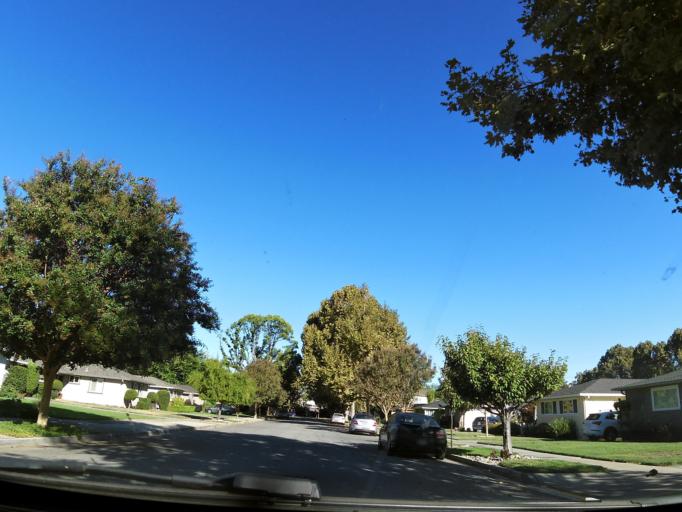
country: US
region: California
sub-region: Santa Clara County
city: Buena Vista
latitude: 37.2866
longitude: -121.9014
